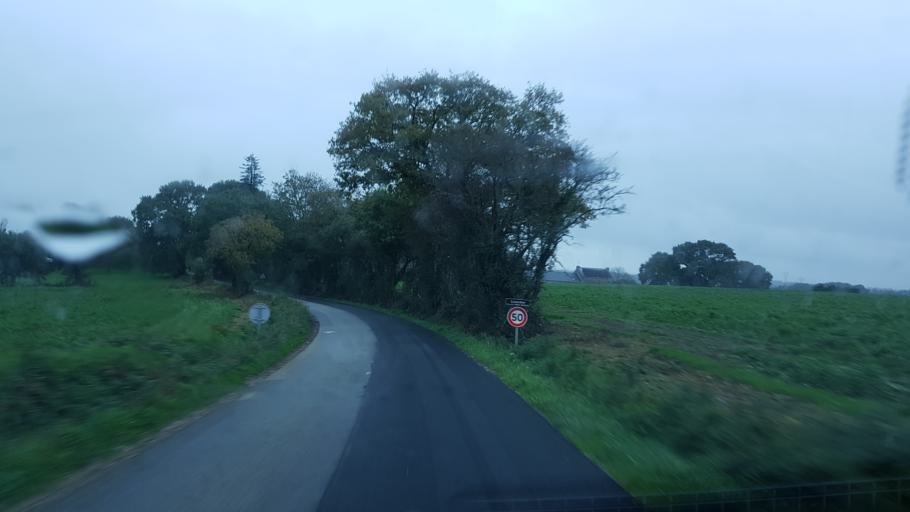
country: FR
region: Brittany
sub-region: Departement du Morbihan
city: Trefflean
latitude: 47.6642
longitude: -2.6201
